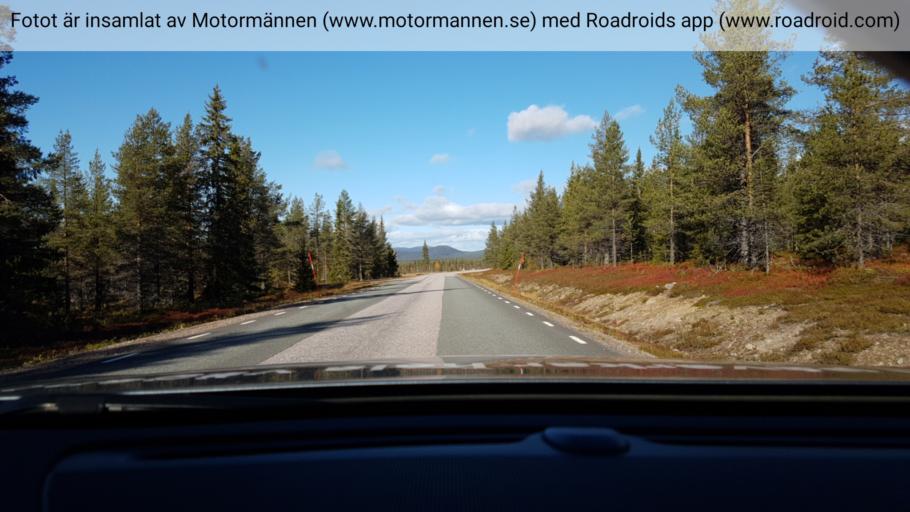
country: SE
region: Norrbotten
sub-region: Arjeplogs Kommun
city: Arjeplog
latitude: 65.8130
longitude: 18.4506
